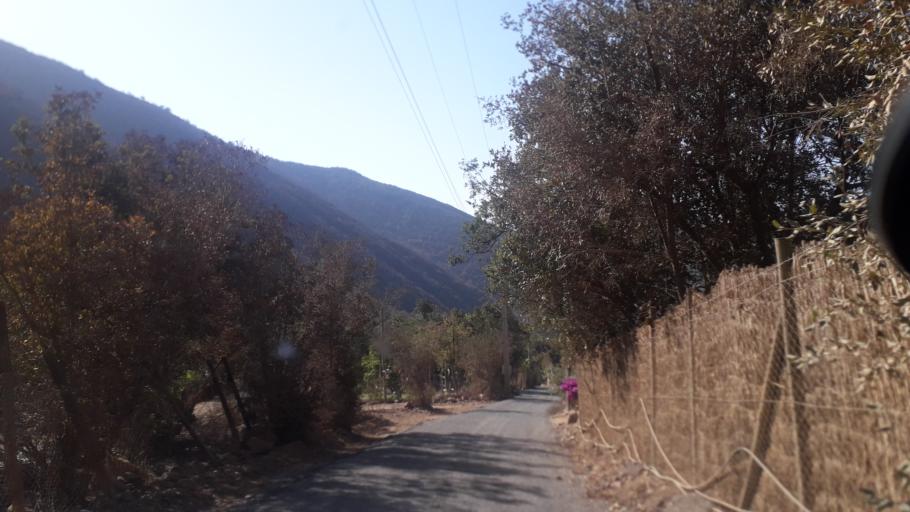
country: CL
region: Valparaiso
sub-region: Provincia de Marga Marga
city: Limache
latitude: -33.0796
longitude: -71.1002
